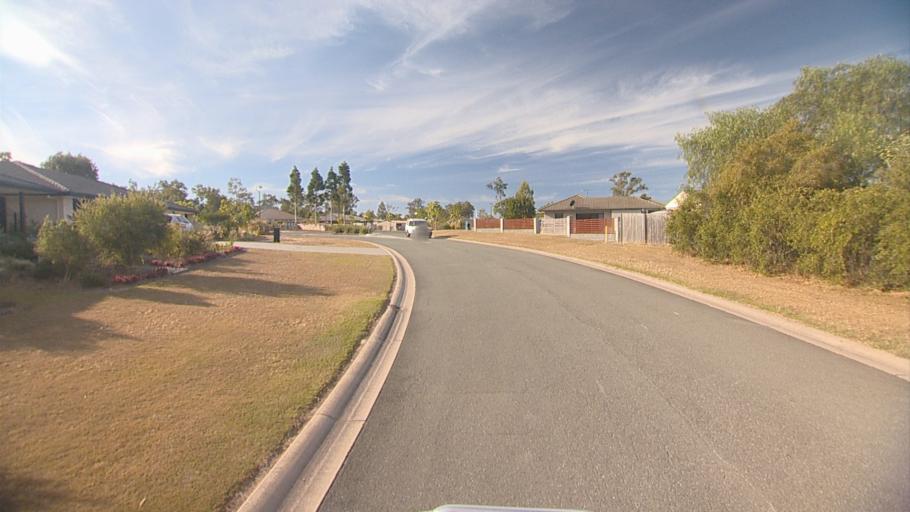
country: AU
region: Queensland
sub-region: Logan
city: North Maclean
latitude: -27.7989
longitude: 152.9587
